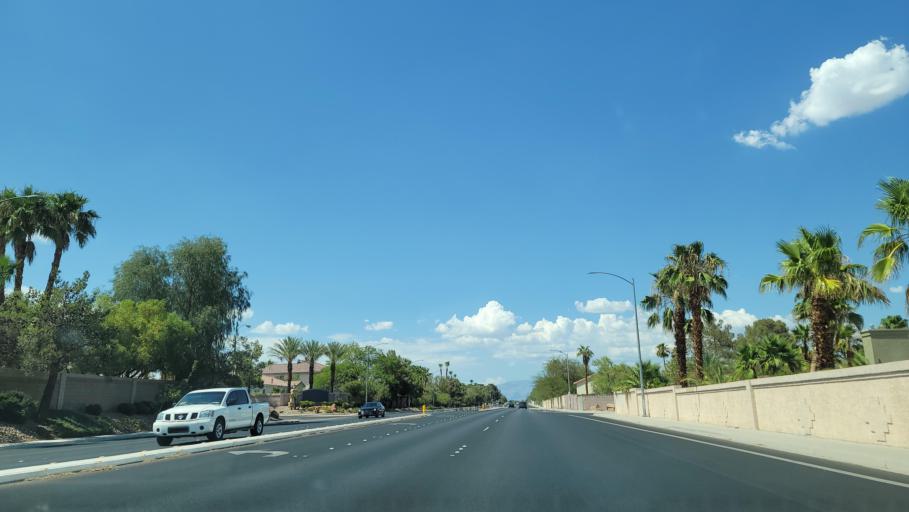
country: US
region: Nevada
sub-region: Clark County
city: Spring Valley
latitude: 36.1320
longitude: -115.2609
